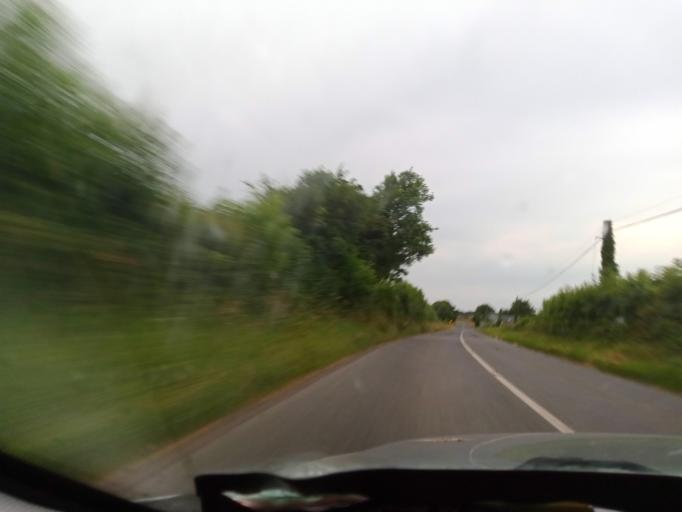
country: IE
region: Leinster
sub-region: Laois
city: Mountmellick
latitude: 53.1258
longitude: -7.3846
